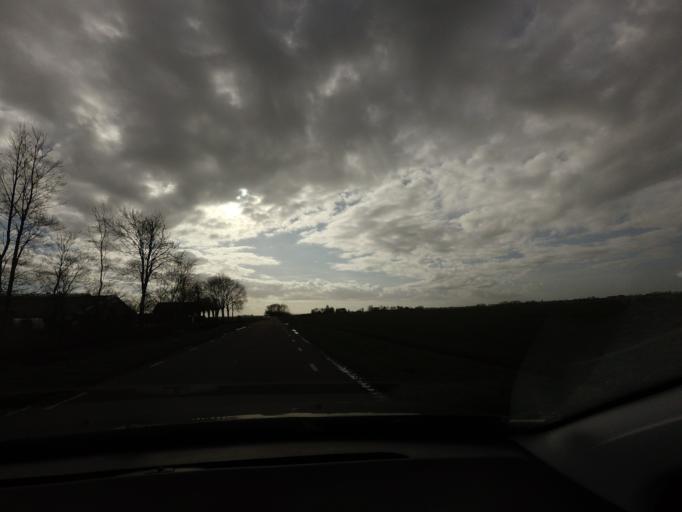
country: NL
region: Friesland
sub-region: Gemeente Boarnsterhim
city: Jirnsum
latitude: 53.0703
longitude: 5.7650
